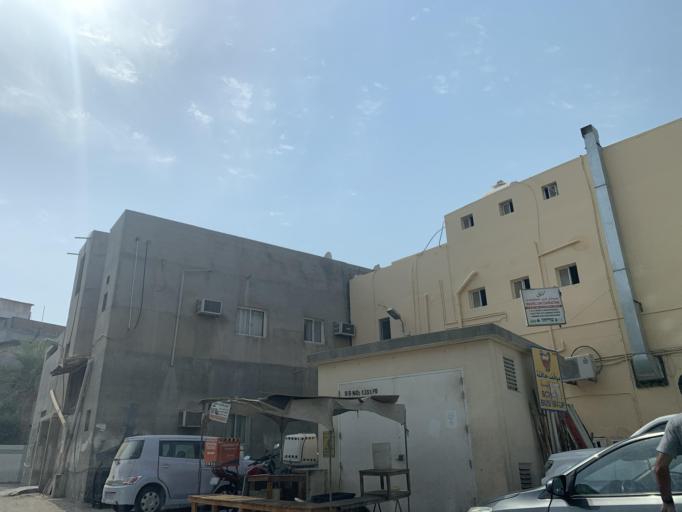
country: BH
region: Manama
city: Jidd Hafs
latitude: 26.2111
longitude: 50.4884
